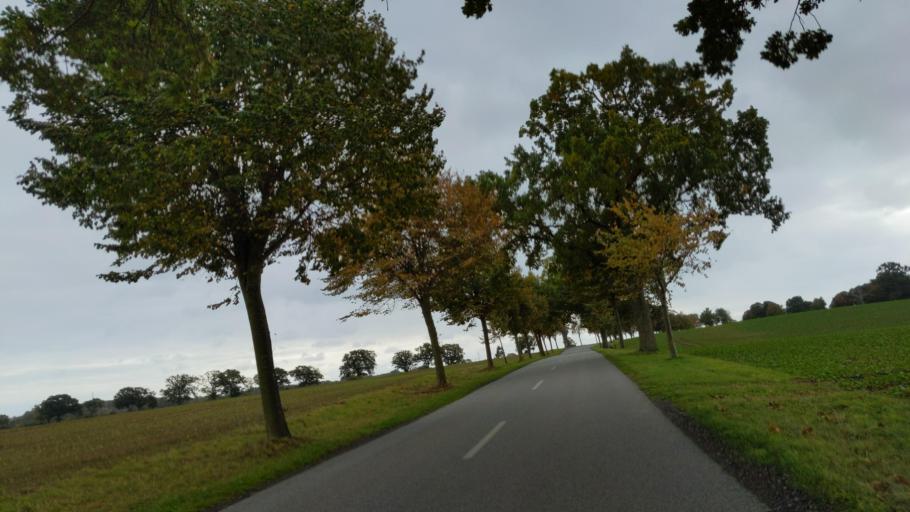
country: DE
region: Schleswig-Holstein
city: Neustadt in Holstein
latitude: 54.1237
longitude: 10.7789
